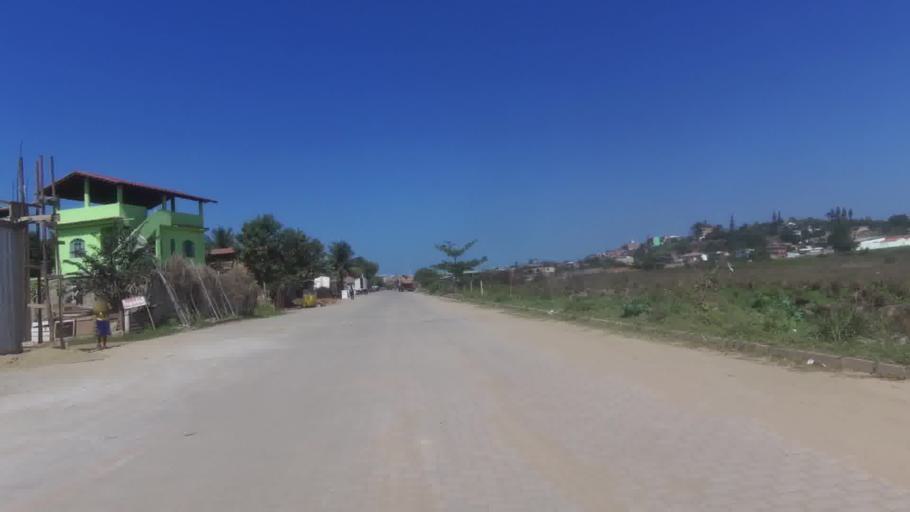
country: BR
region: Espirito Santo
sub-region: Itapemirim
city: Itapemirim
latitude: -21.0146
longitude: -40.8163
